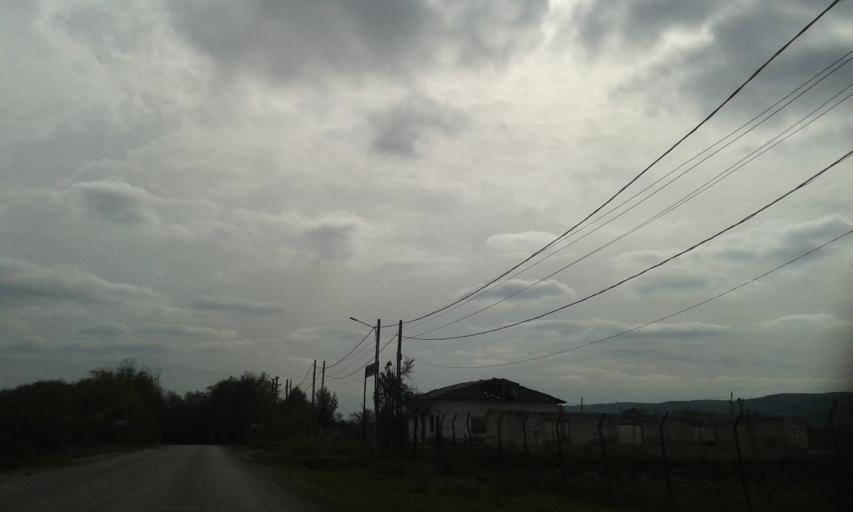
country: RO
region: Gorj
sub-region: Comuna Targu Carbunesti
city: Pojogeni
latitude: 44.9881
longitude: 23.4965
